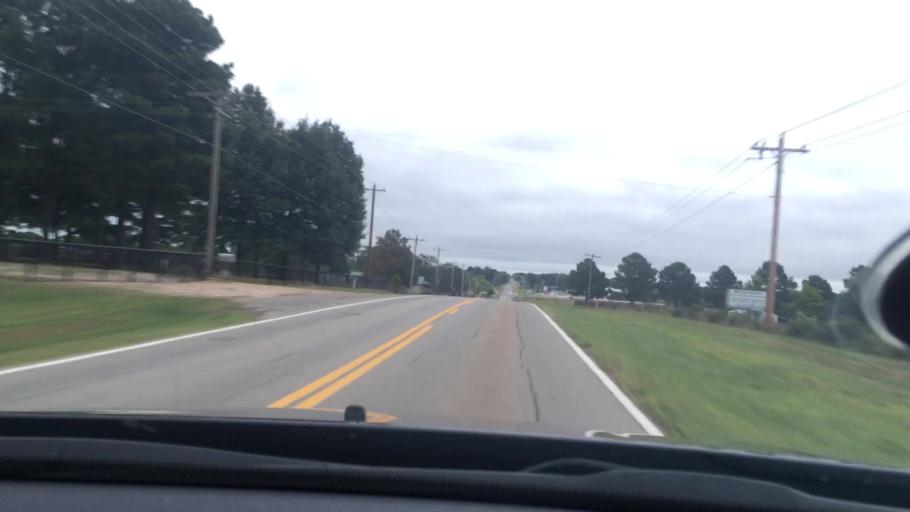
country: US
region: Oklahoma
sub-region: Sequoyah County
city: Vian
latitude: 35.6097
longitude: -94.9834
